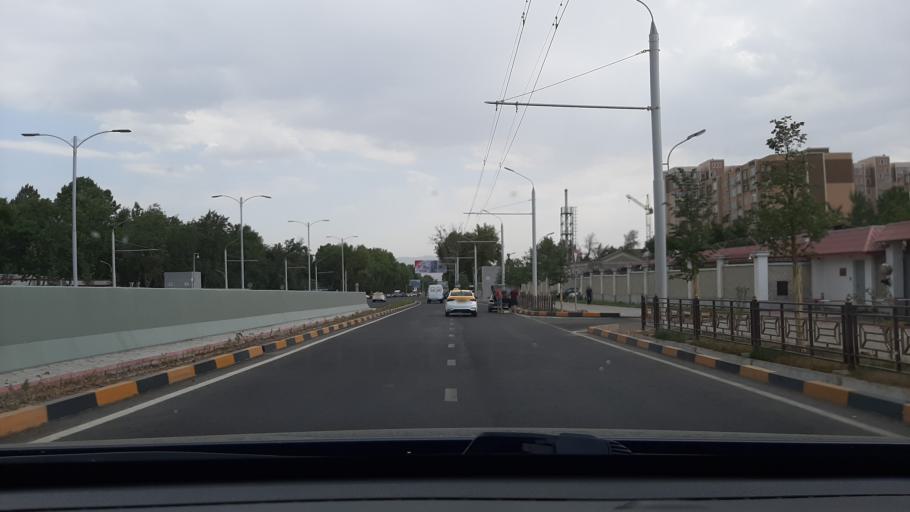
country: TJ
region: Dushanbe
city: Dushanbe
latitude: 38.5832
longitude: 68.7549
